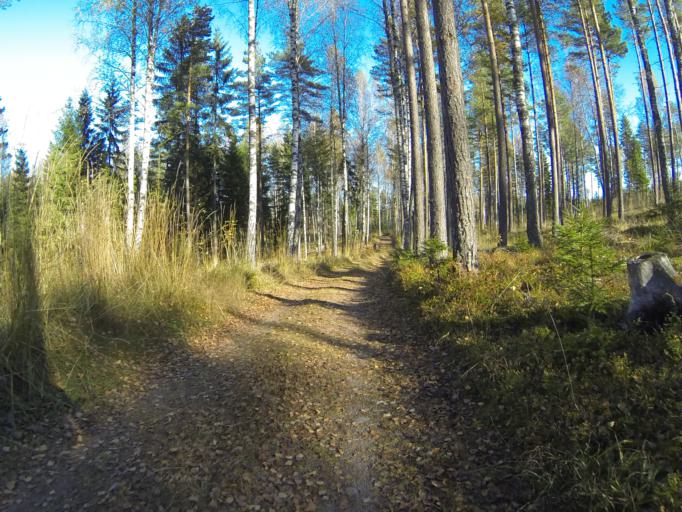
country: FI
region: Varsinais-Suomi
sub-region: Salo
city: Saerkisalo
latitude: 60.2141
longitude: 22.9765
